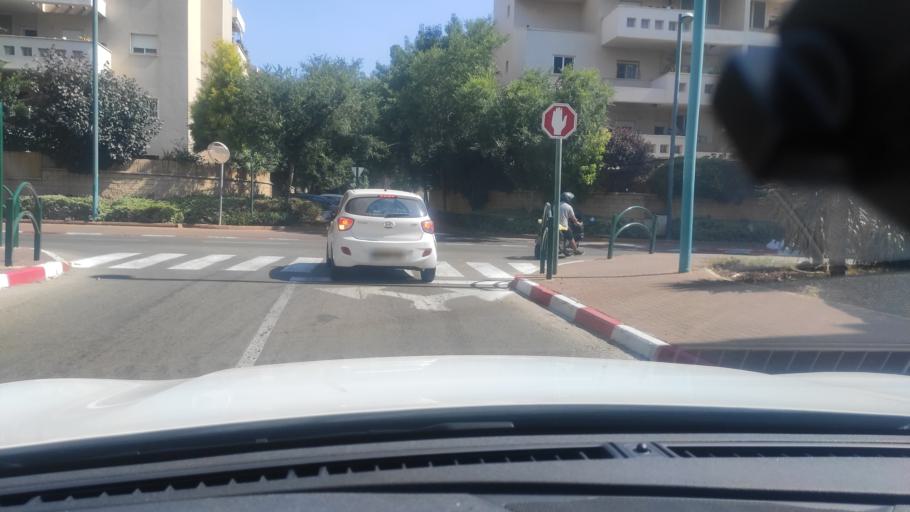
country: IL
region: Central District
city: Kfar Saba
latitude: 32.1791
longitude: 34.9324
